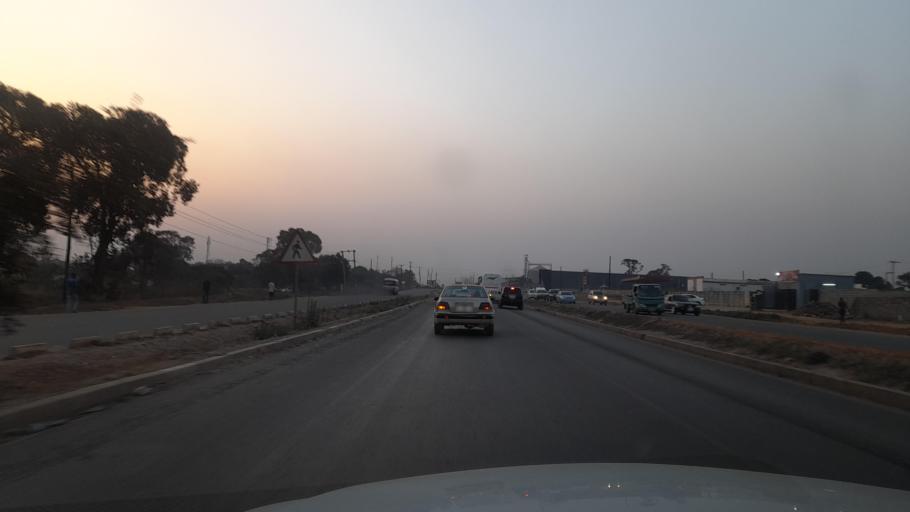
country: ZM
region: Copperbelt
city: Kitwe
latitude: -12.7808
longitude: 28.1956
